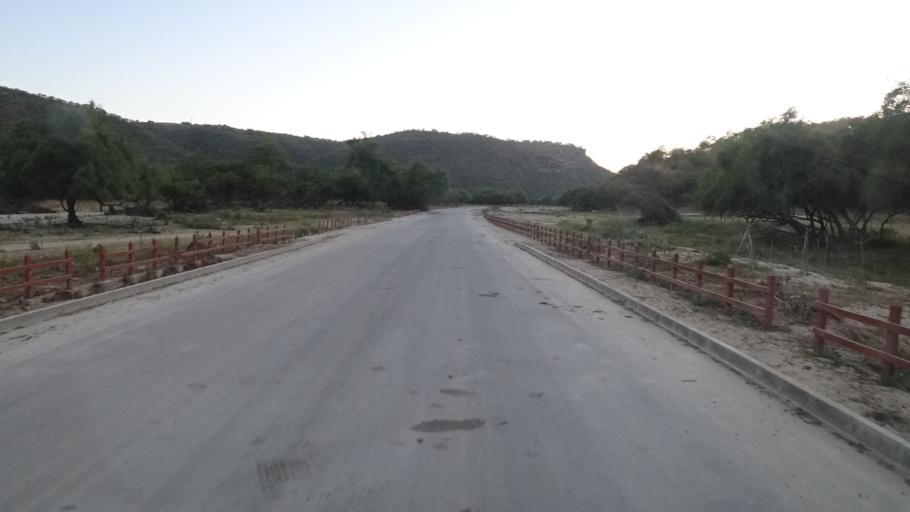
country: OM
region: Zufar
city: Salalah
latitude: 17.0934
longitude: 54.4475
